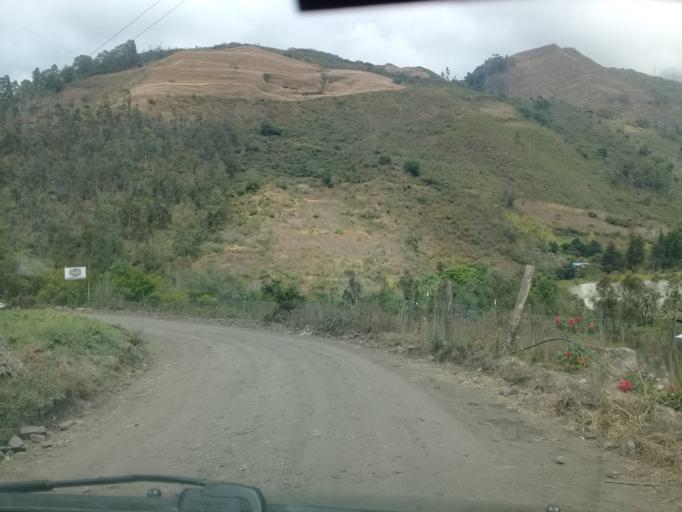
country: CO
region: Cundinamarca
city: Caqueza
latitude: 4.4164
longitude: -73.9841
